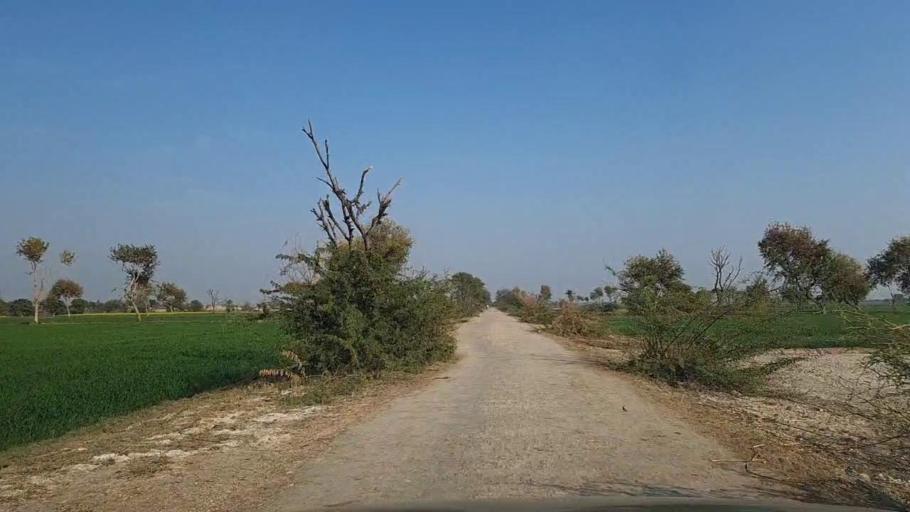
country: PK
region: Sindh
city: Nawabshah
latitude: 26.3874
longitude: 68.4560
